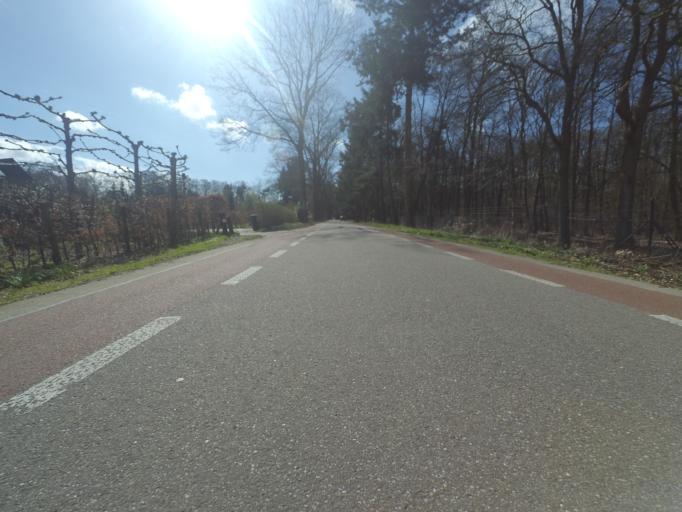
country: NL
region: Gelderland
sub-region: Gemeente Apeldoorn
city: Beekbergen
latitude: 52.1096
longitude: 5.8765
